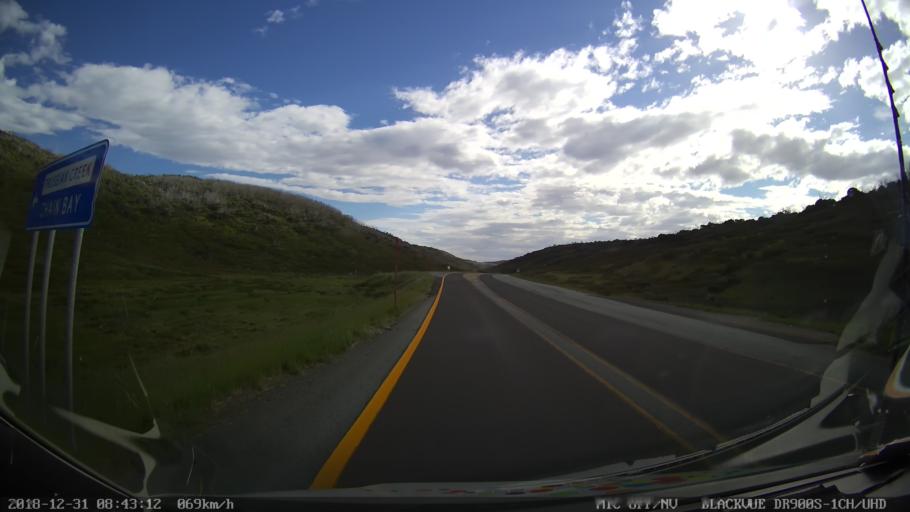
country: AU
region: New South Wales
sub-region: Snowy River
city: Jindabyne
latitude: -36.3906
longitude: 148.4418
